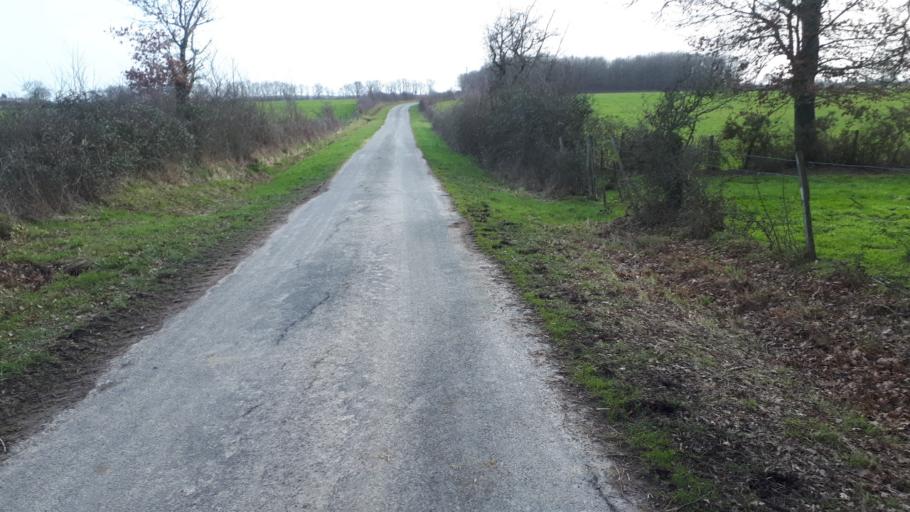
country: FR
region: Poitou-Charentes
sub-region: Departement de la Vienne
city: Archigny
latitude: 46.6239
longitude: 0.7456
